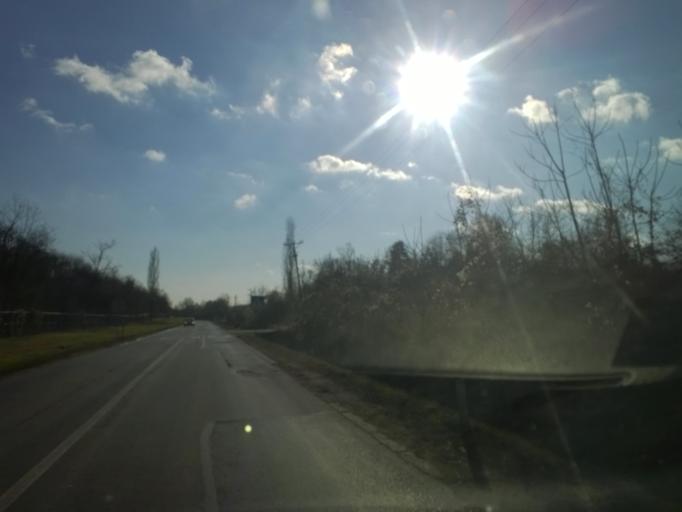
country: RS
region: Central Serbia
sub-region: Podunavski Okrug
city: Smederevo
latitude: 44.6011
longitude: 20.9635
